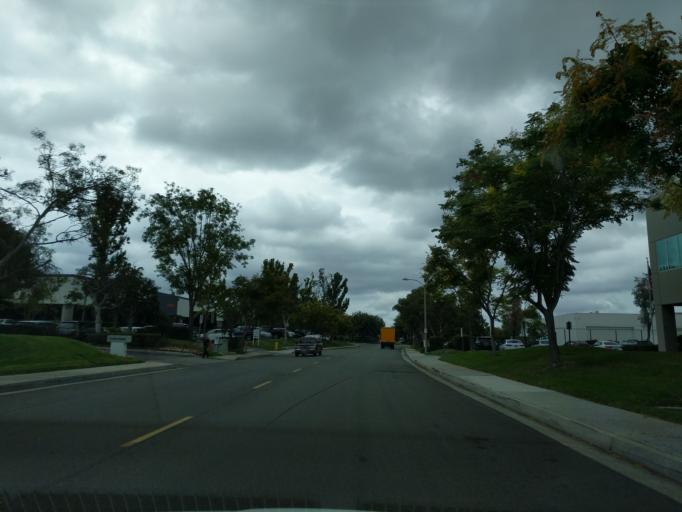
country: US
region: California
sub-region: Orange County
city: Lake Forest
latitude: 33.6474
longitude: -117.7122
